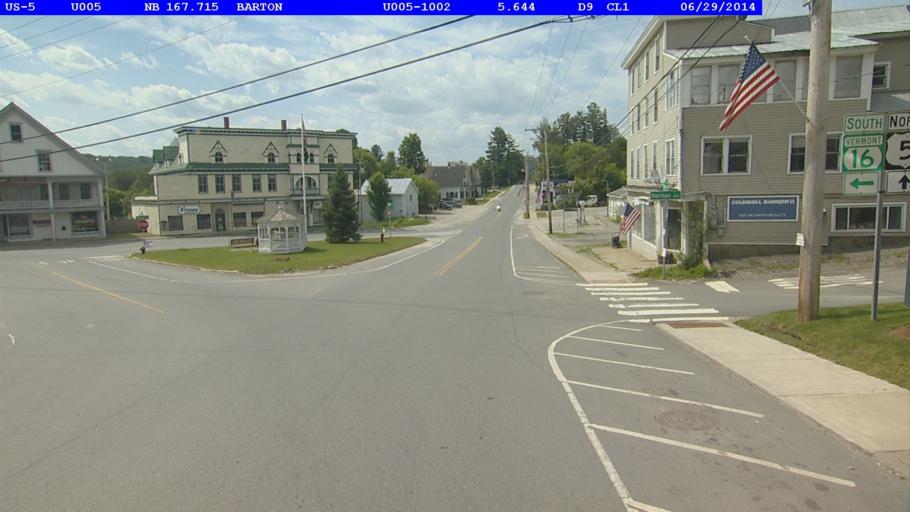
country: US
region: Vermont
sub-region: Orleans County
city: Newport
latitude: 44.7505
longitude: -72.1794
